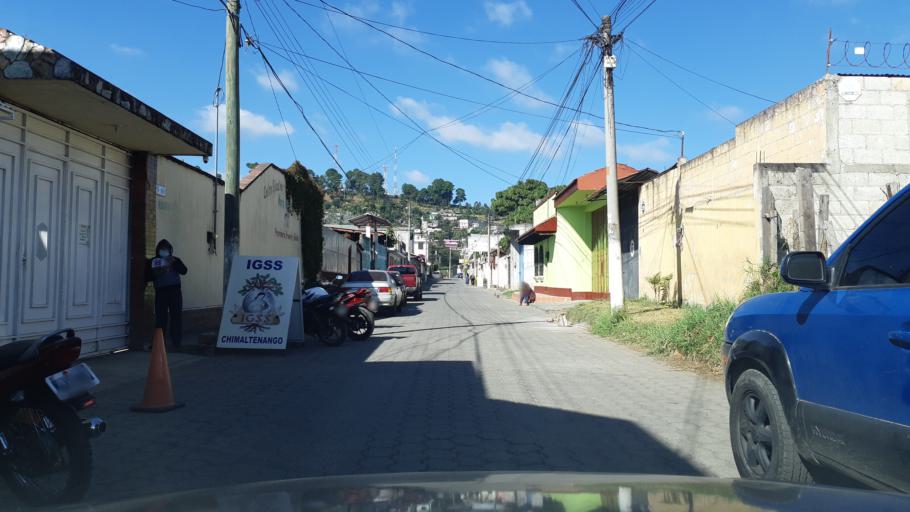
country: GT
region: Chimaltenango
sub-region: Municipio de Chimaltenango
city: Chimaltenango
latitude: 14.6516
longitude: -90.8161
